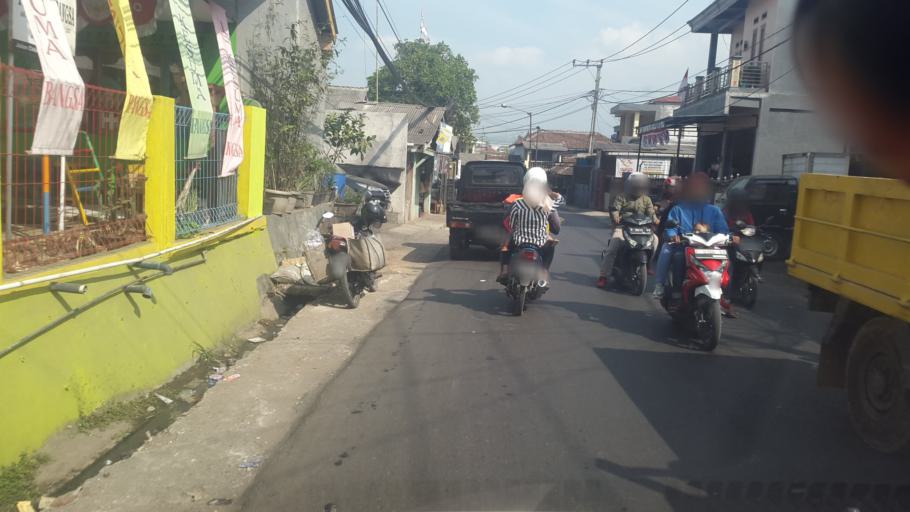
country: ID
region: West Java
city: Cicurug
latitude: -6.7969
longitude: 106.7764
